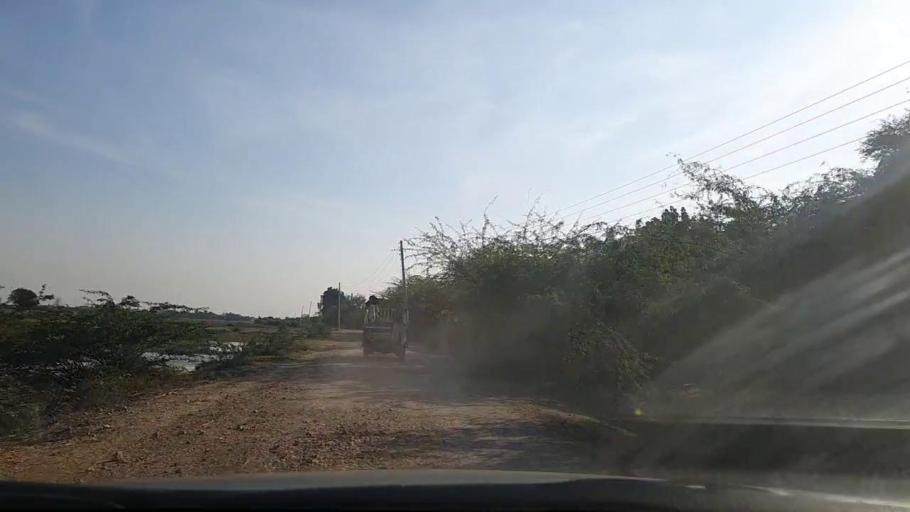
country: PK
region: Sindh
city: Mirpur Sakro
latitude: 24.5330
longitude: 67.6329
